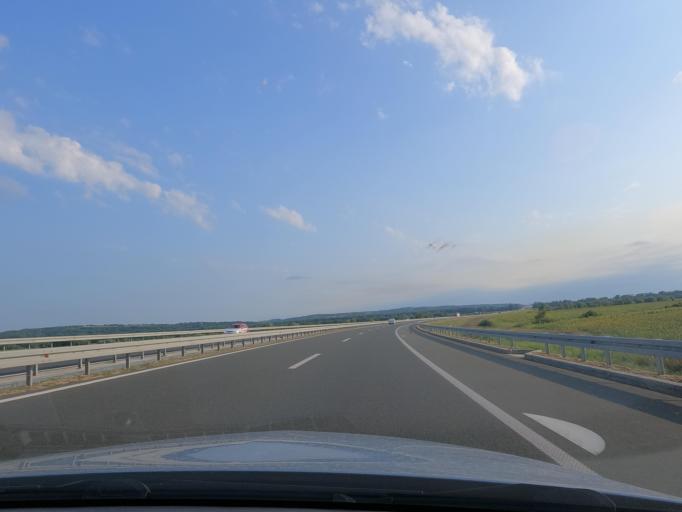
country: RS
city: Baric
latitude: 44.6884
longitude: 20.2652
